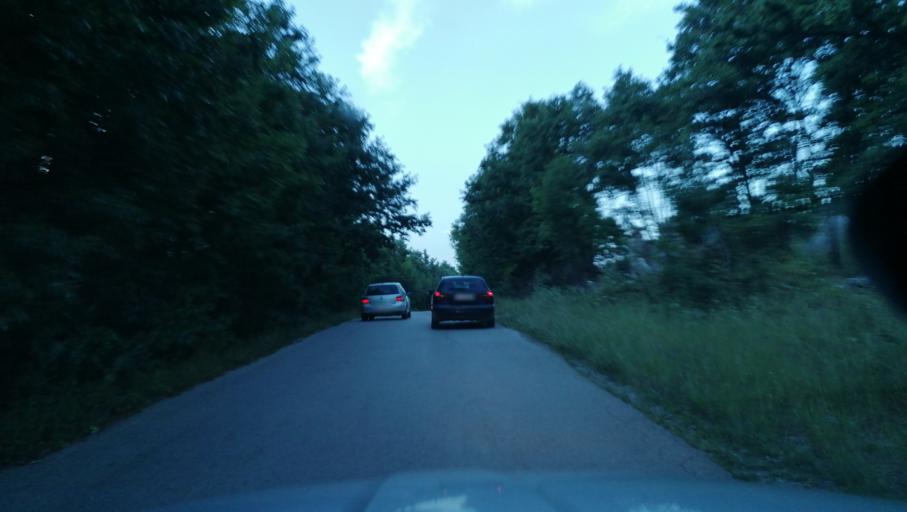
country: RS
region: Central Serbia
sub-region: Kolubarski Okrug
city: Valjevo
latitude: 44.2401
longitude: 19.8607
